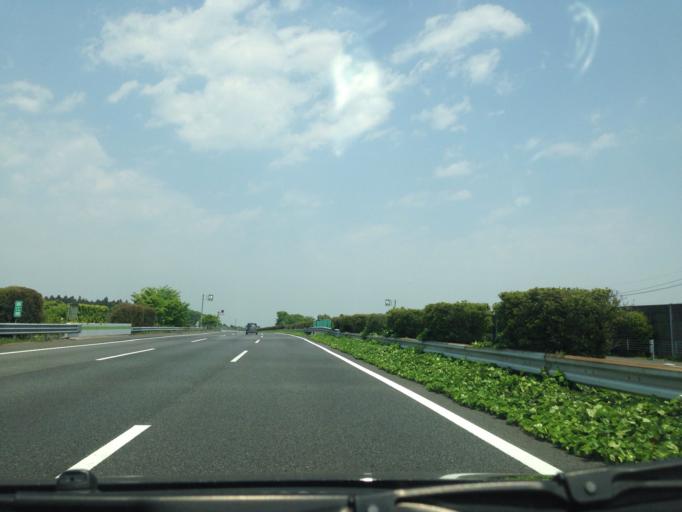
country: JP
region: Tochigi
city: Kanuma
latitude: 36.5060
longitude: 139.7676
